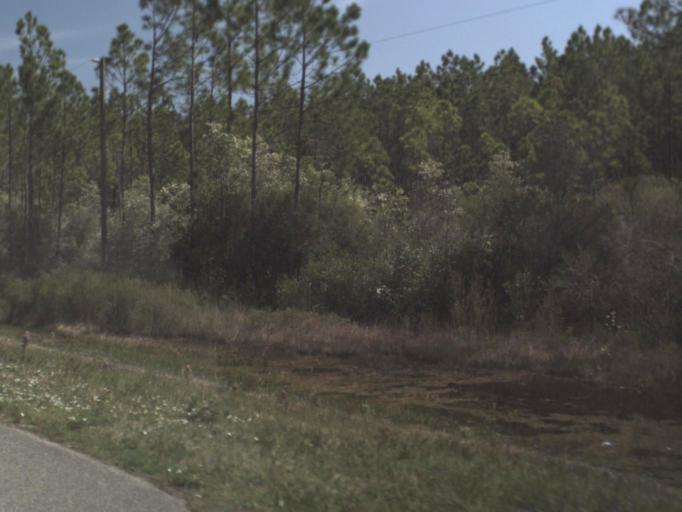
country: US
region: Florida
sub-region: Gulf County
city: Port Saint Joe
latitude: 29.7362
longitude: -85.1639
